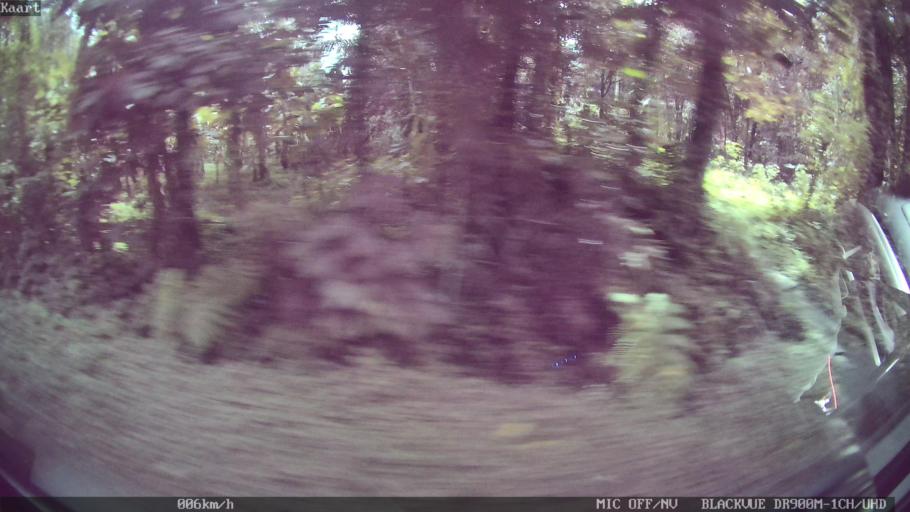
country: ID
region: Bali
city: Bunutan
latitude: -8.4696
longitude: 115.2346
